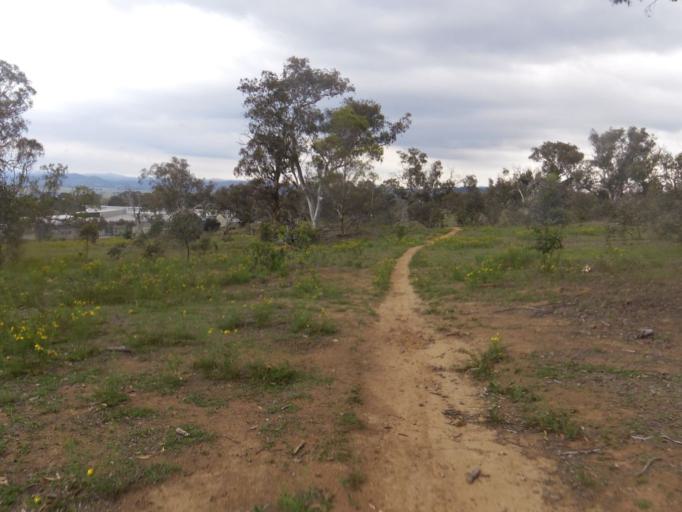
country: AU
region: Australian Capital Territory
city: Forrest
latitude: -35.3460
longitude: 149.1349
